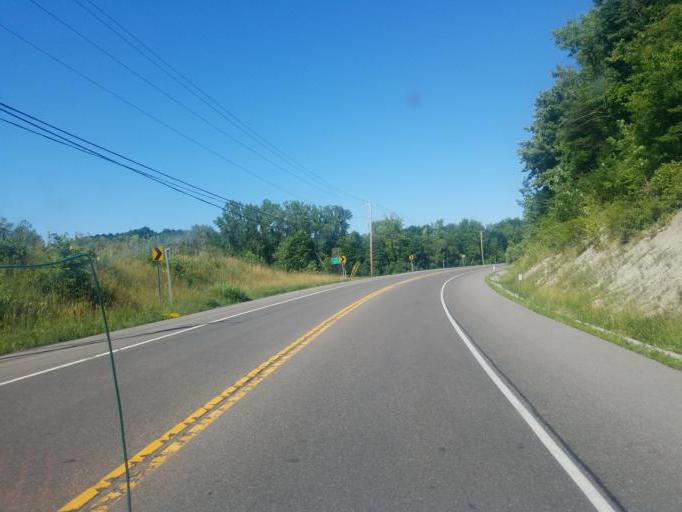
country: US
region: New York
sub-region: Wayne County
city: Lyons
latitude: 43.0671
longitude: -77.0372
